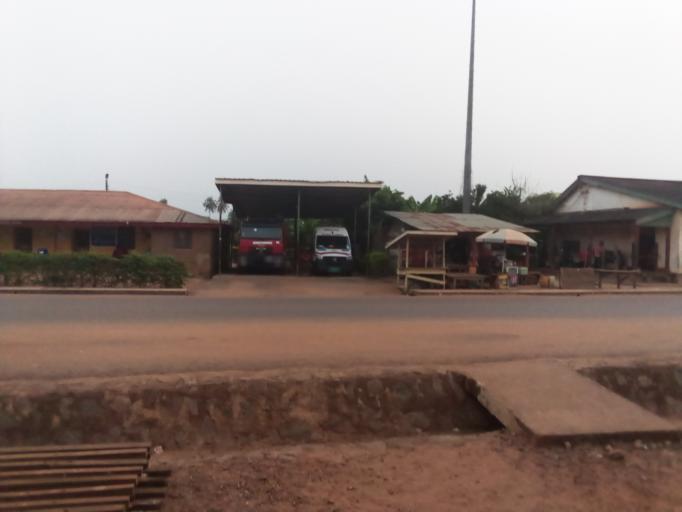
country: CI
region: Sud-Comoe
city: Ayame
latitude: 5.8217
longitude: -2.8235
